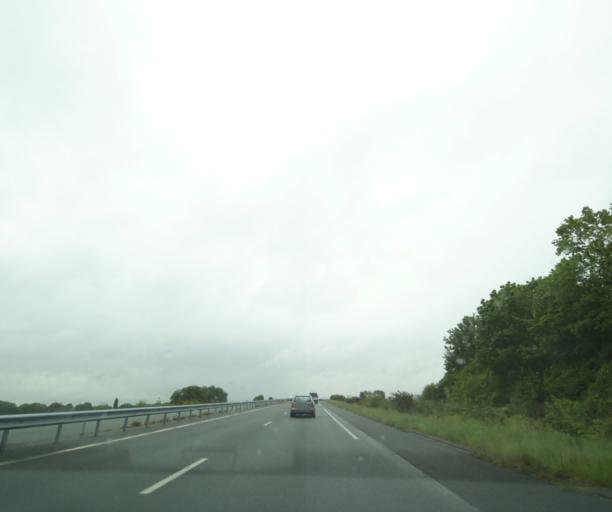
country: FR
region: Poitou-Charentes
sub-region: Departement de la Charente-Maritime
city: Nieul-les-Saintes
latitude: 45.7003
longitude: -0.7512
